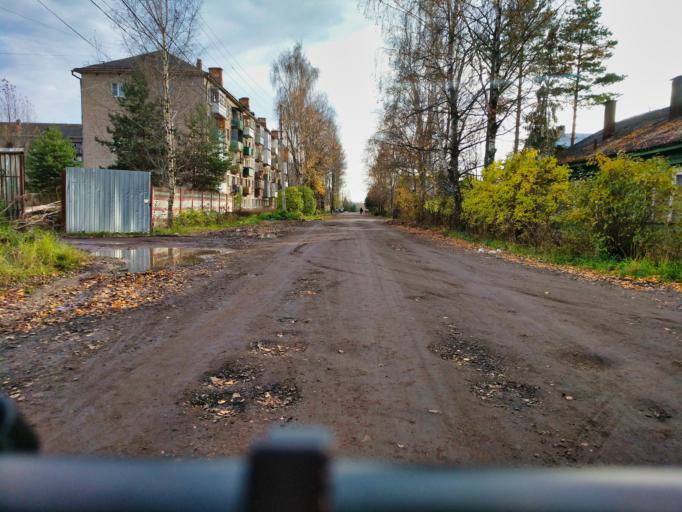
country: RU
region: Tverskaya
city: Rzhev
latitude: 56.2661
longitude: 34.3257
